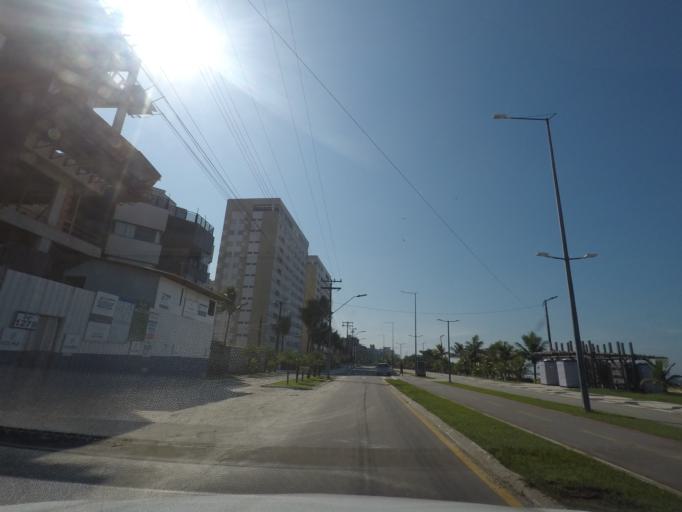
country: BR
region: Parana
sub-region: Guaratuba
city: Guaratuba
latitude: -25.8342
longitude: -48.5373
